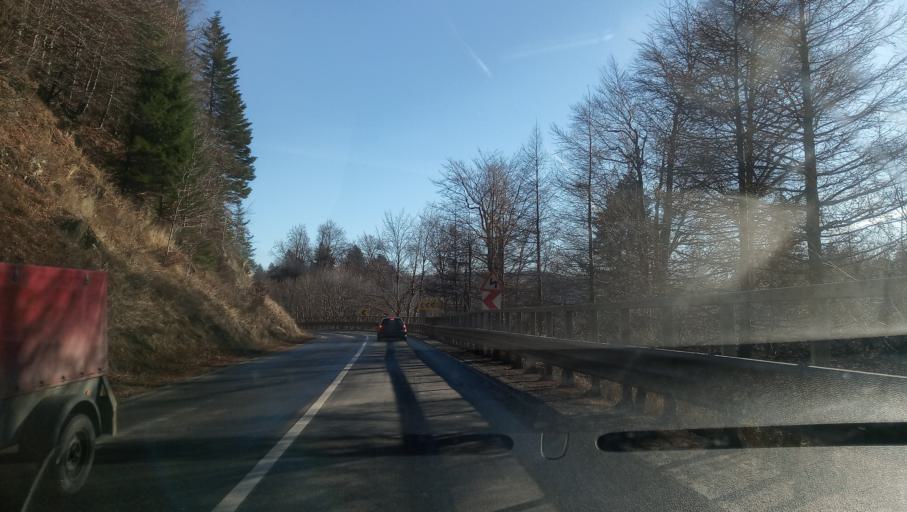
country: RO
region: Brasov
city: Crivina
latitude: 45.4704
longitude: 25.9225
